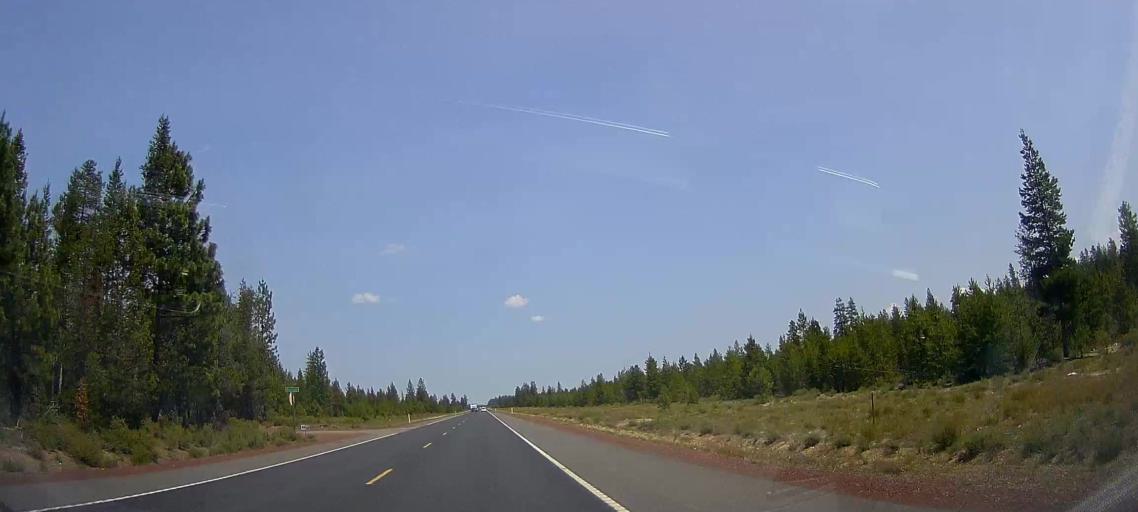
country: US
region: Oregon
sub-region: Deschutes County
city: La Pine
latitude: 43.4958
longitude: -121.6736
